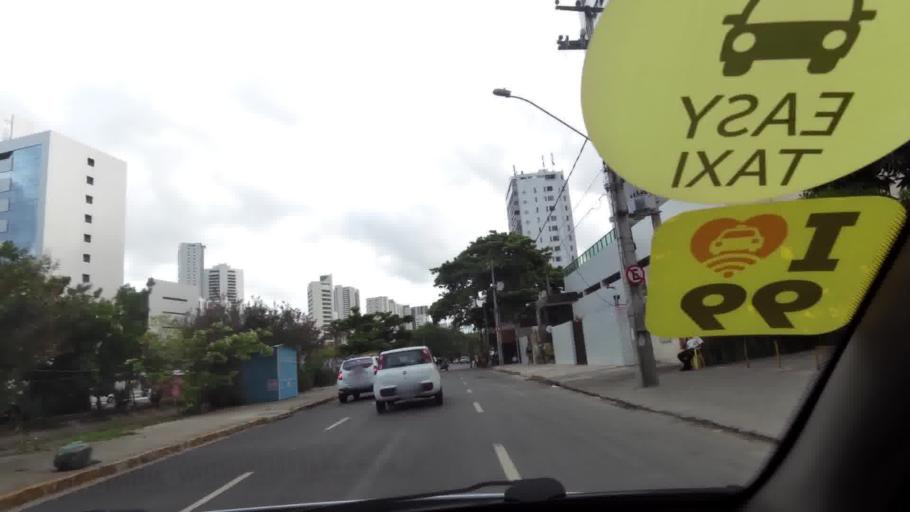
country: BR
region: Pernambuco
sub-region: Recife
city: Recife
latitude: -8.1280
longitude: -34.9027
